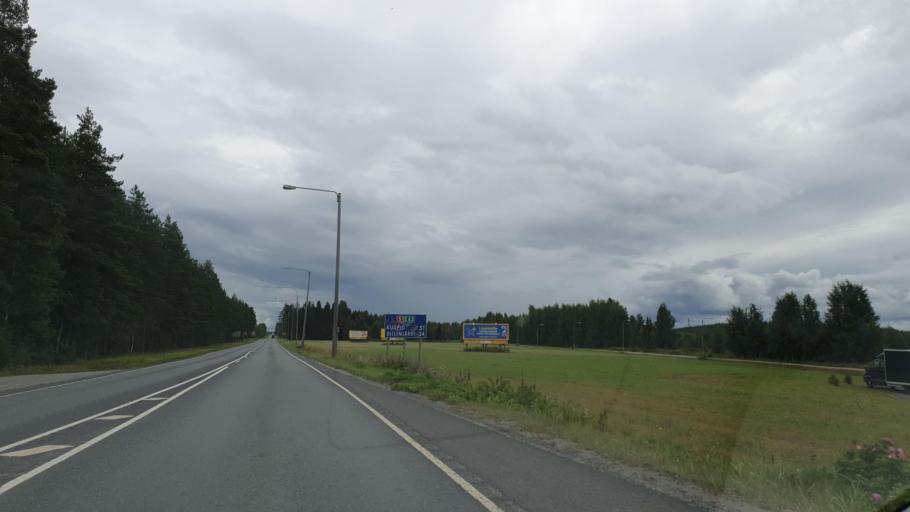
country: FI
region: Northern Savo
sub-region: Ylae-Savo
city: Lapinlahti
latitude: 63.3454
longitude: 27.4163
